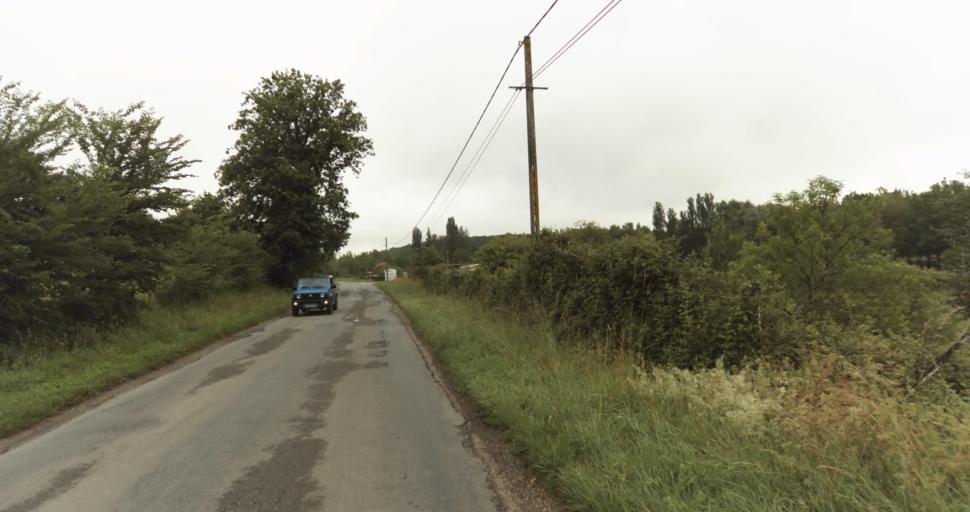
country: FR
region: Aquitaine
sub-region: Departement de la Dordogne
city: Lalinde
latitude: 44.8511
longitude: 0.7763
